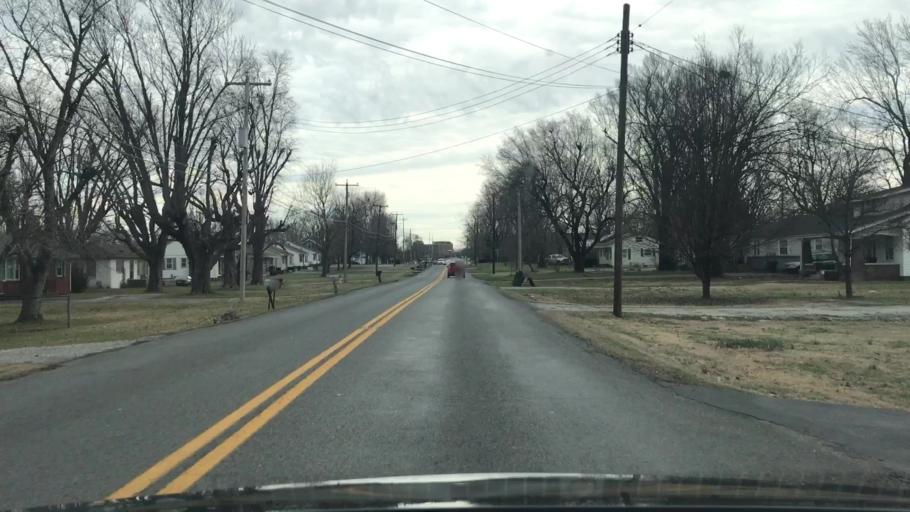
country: US
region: Kentucky
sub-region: Christian County
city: Hopkinsville
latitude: 36.8606
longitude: -87.5091
